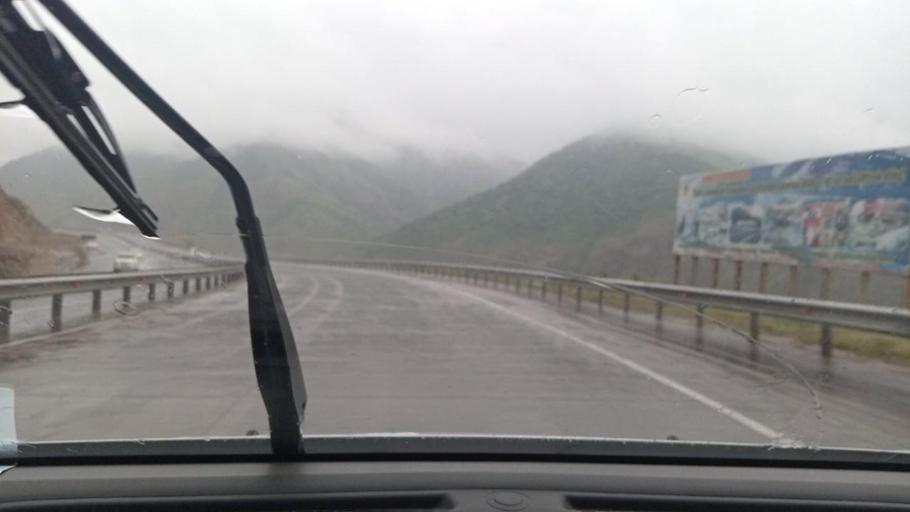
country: UZ
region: Toshkent
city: Angren
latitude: 41.0725
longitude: 70.2700
